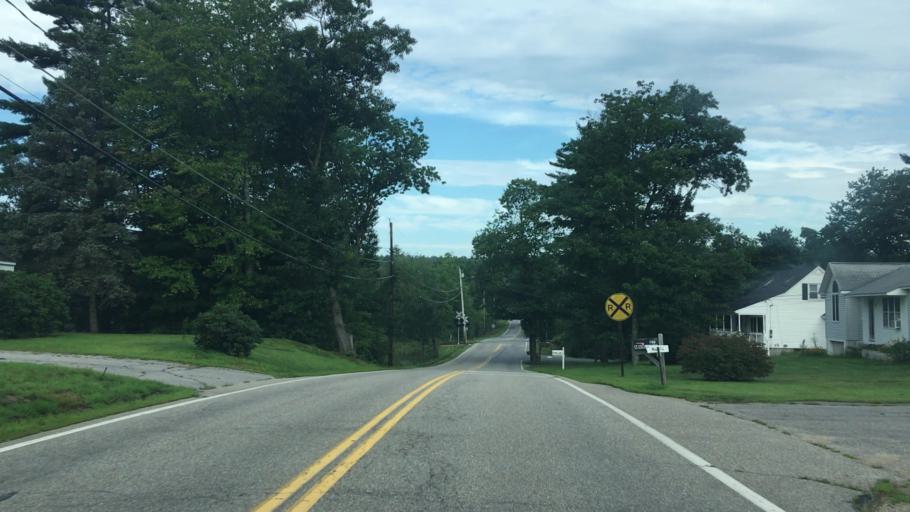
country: US
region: New Hampshire
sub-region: Strafford County
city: Rochester
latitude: 43.3498
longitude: -70.9788
